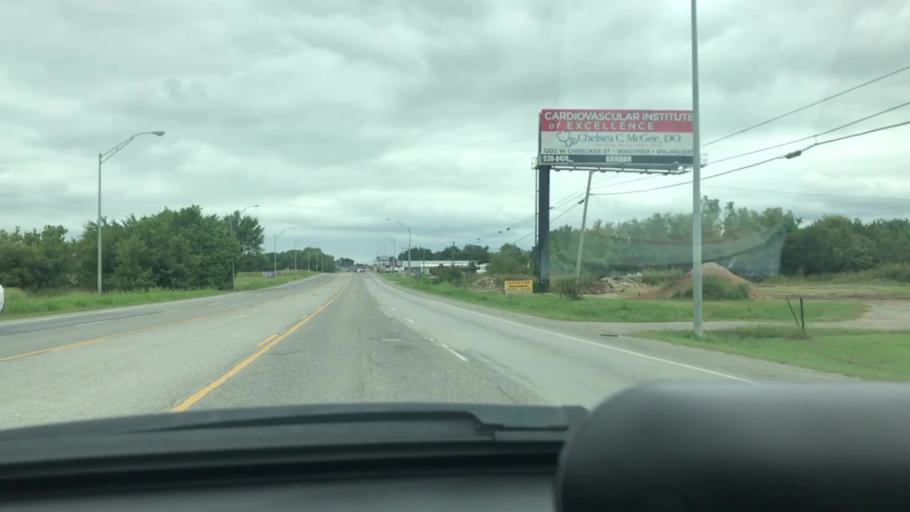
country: US
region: Oklahoma
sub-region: Wagoner County
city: Wagoner
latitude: 35.9490
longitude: -95.3952
